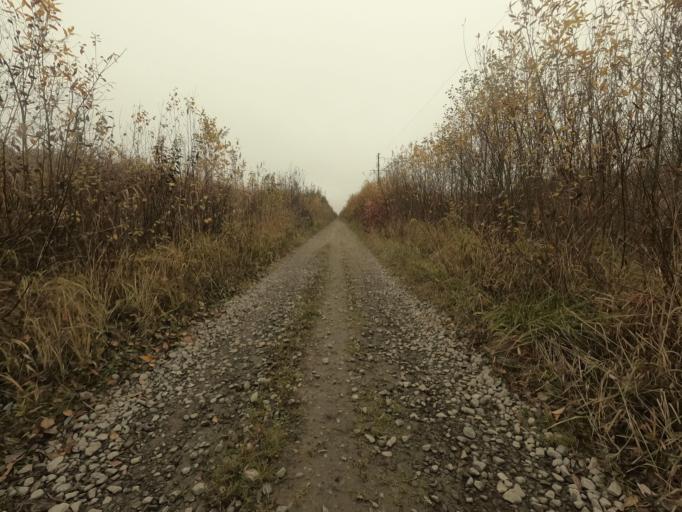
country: RU
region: Leningrad
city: Pavlovo
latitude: 59.7671
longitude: 30.9429
